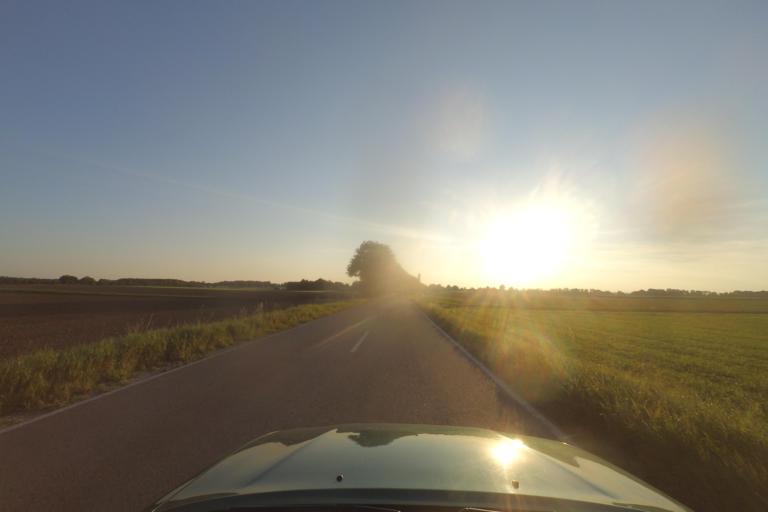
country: DE
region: Bavaria
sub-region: Upper Bavaria
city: Kaufering
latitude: 48.0936
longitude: 10.8929
